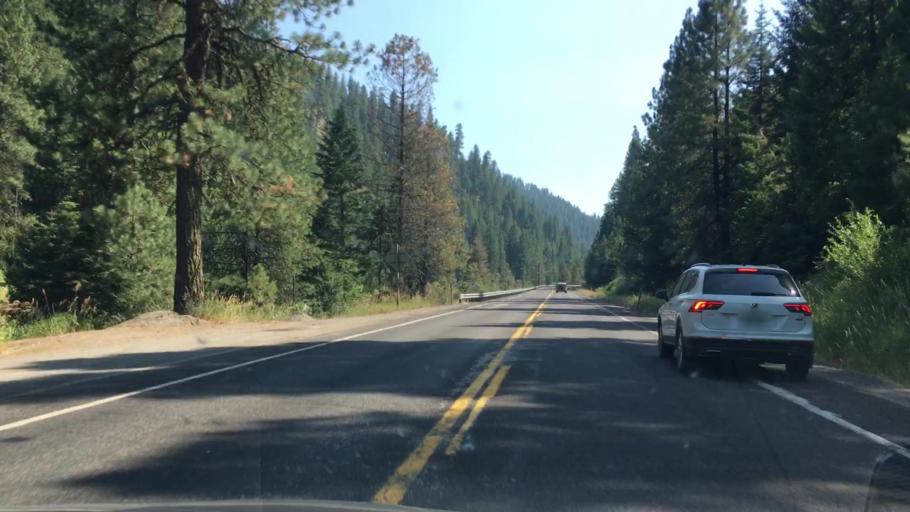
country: US
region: Idaho
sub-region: Valley County
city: Cascade
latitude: 44.2424
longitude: -116.1031
